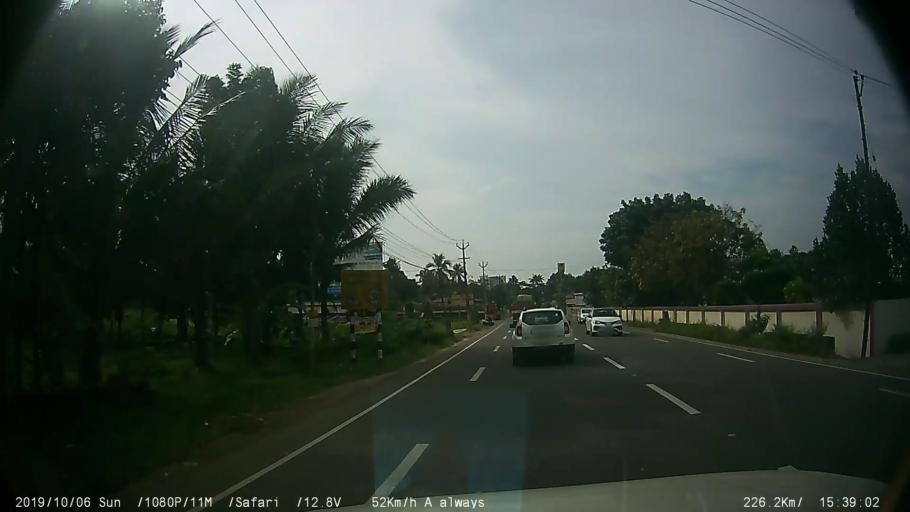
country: IN
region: Kerala
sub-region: Ernakulam
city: Perumpavur
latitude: 10.1574
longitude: 76.4449
